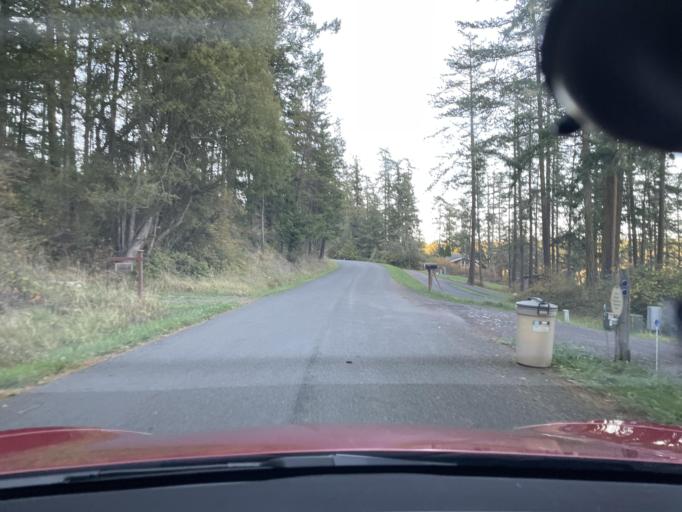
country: US
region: Washington
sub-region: San Juan County
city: Friday Harbor
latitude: 48.6054
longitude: -123.1478
